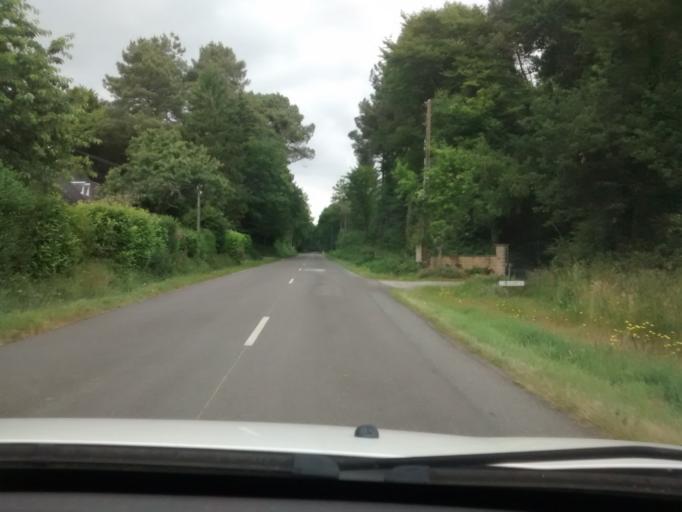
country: FR
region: Brittany
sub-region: Departement d'Ille-et-Vilaine
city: Servon-sur-Vilaine
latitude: 48.1403
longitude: -1.4511
